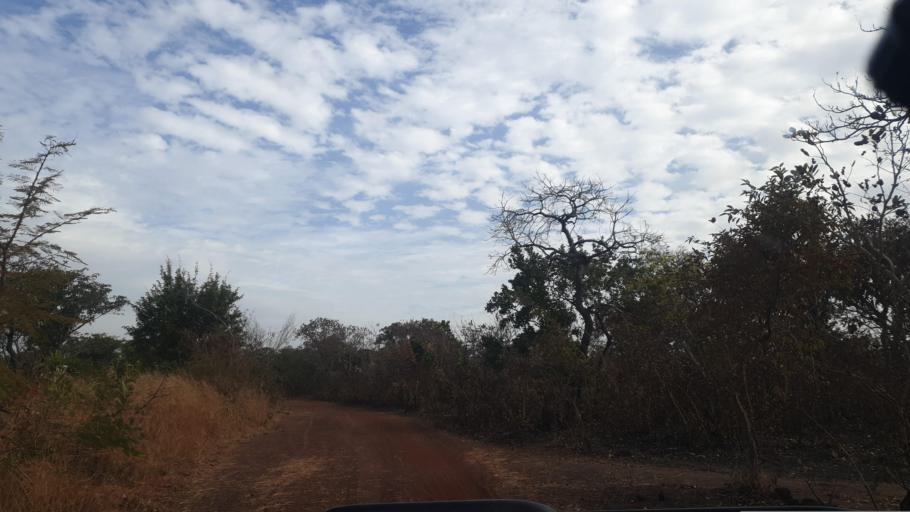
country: ML
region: Sikasso
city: Yanfolila
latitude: 11.3932
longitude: -8.0209
